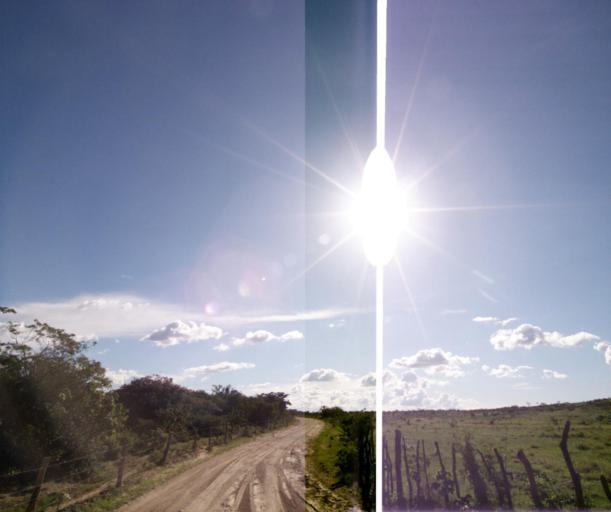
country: BR
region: Bahia
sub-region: Tanhacu
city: Tanhacu
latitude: -14.1887
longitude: -40.9655
